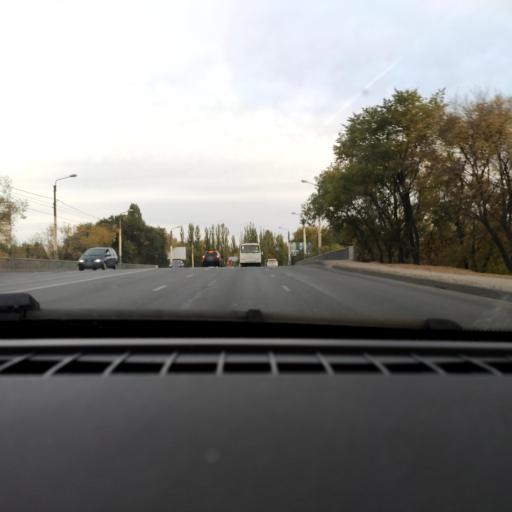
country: RU
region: Voronezj
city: Maslovka
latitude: 51.6229
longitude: 39.2343
